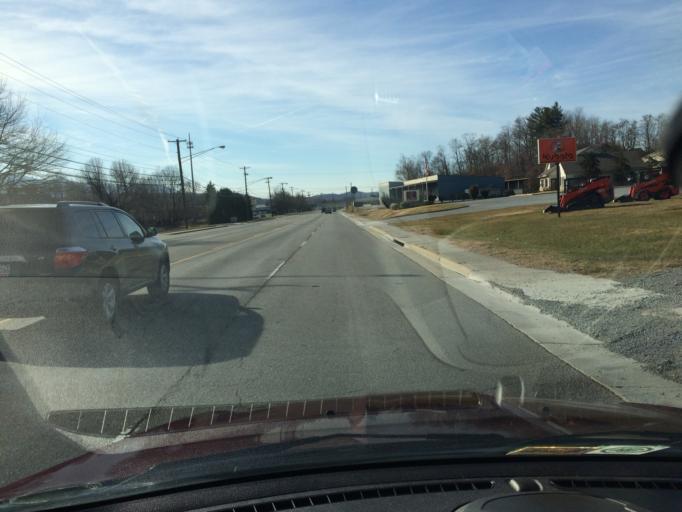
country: US
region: Virginia
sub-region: City of Salem
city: Salem
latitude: 37.2848
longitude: -80.1006
